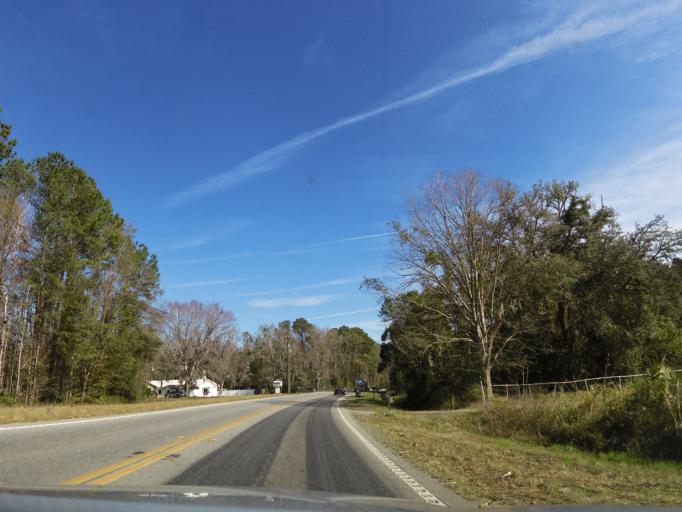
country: US
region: Georgia
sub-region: Glynn County
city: Dock Junction
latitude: 31.2739
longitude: -81.5782
